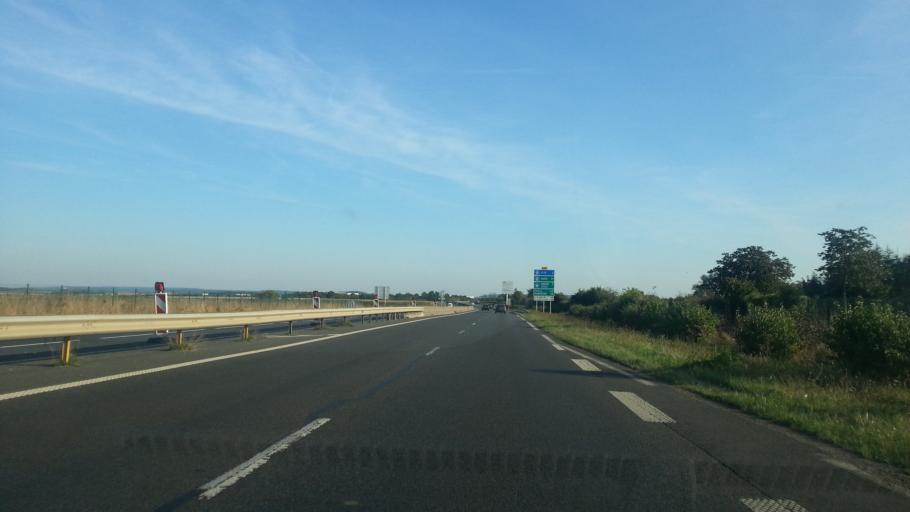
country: FR
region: Picardie
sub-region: Departement de l'Oise
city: Tille
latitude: 49.4491
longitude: 2.1033
